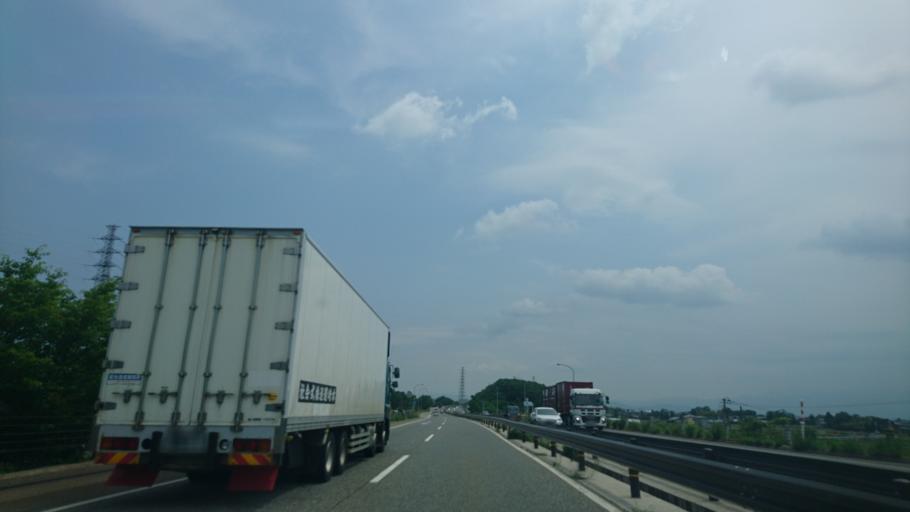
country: JP
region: Niigata
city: Suibara
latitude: 37.9533
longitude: 139.2152
